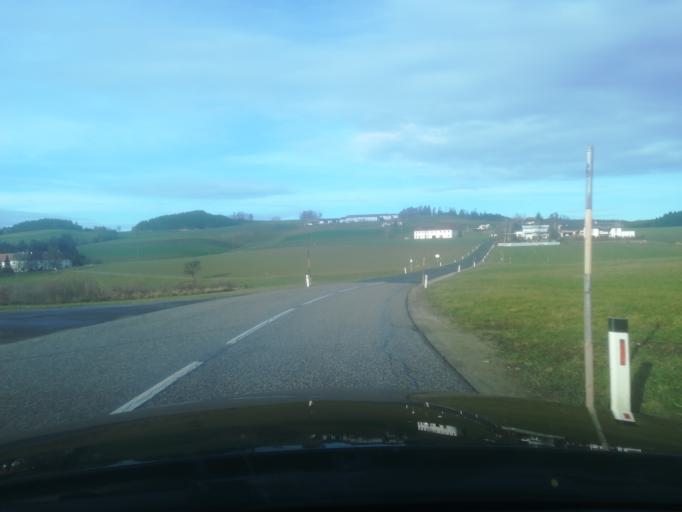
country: AT
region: Upper Austria
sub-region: Politischer Bezirk Perg
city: Perg
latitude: 48.3382
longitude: 14.6220
